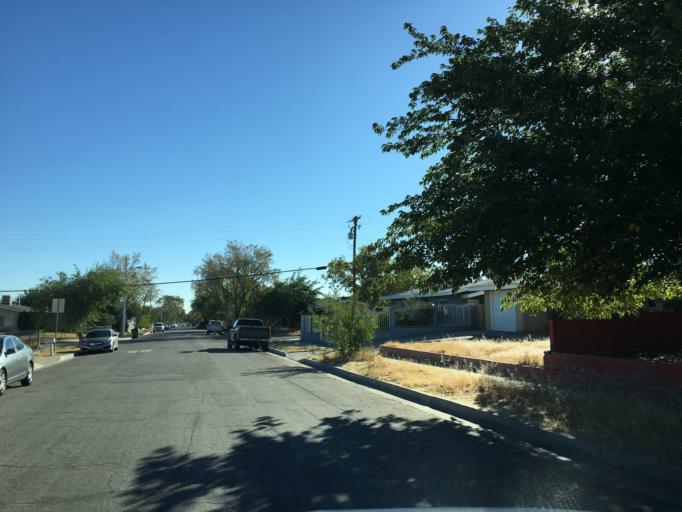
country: US
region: California
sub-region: Los Angeles County
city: Desert View Highlands
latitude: 34.5895
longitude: -118.1559
